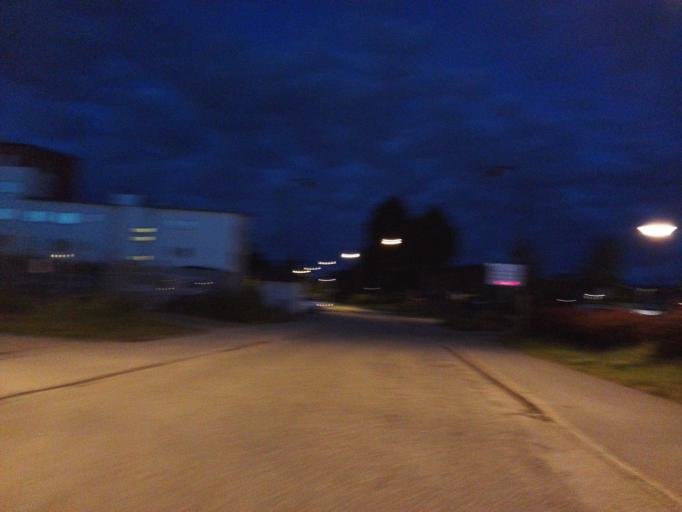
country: SE
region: Stockholm
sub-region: Huddinge Kommun
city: Segeltorp
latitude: 59.2832
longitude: 17.9339
